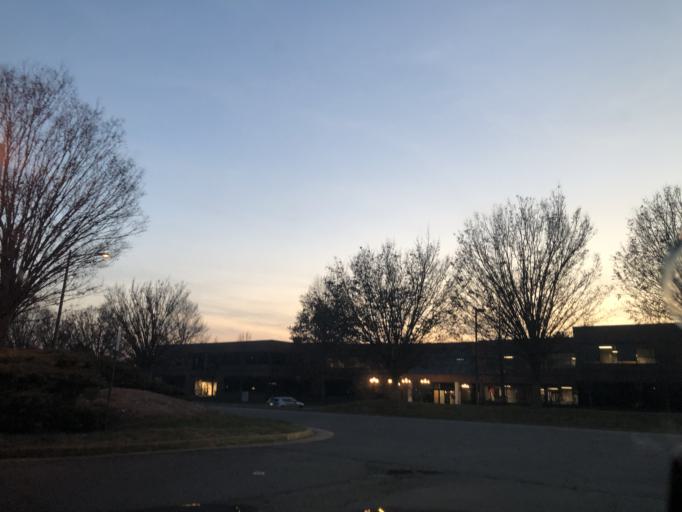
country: US
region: Virginia
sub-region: Loudoun County
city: Leesburg
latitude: 39.0834
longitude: -77.5558
